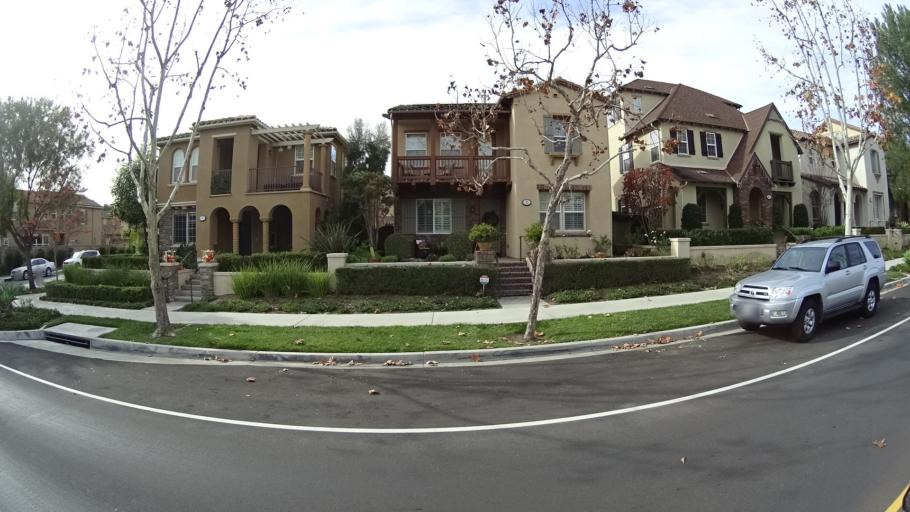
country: US
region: California
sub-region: Orange County
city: Laguna Woods
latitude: 33.5979
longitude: -117.7257
